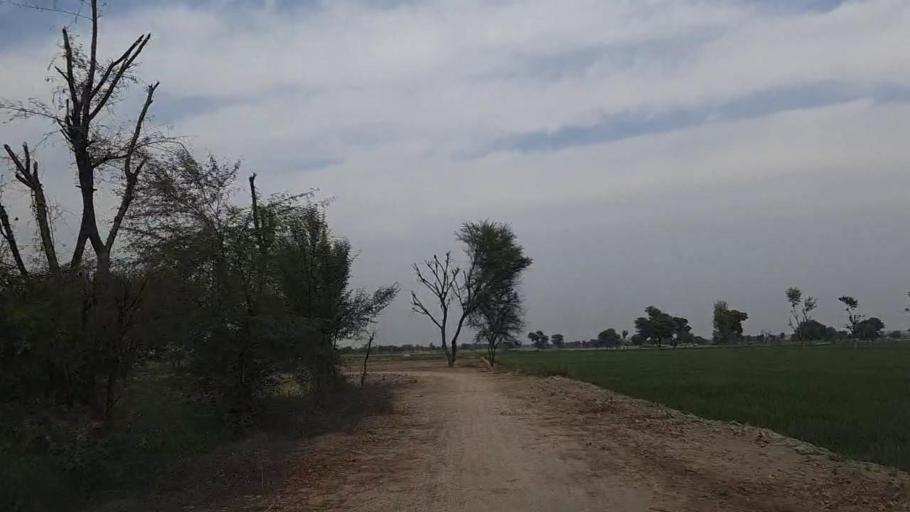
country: PK
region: Sindh
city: Daur
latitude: 26.4409
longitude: 68.4710
